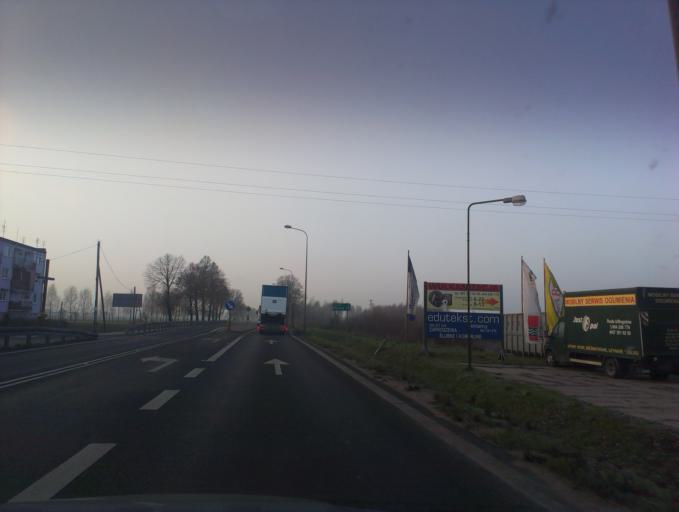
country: PL
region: Greater Poland Voivodeship
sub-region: Powiat obornicki
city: Rogozno
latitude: 52.7587
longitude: 16.9642
